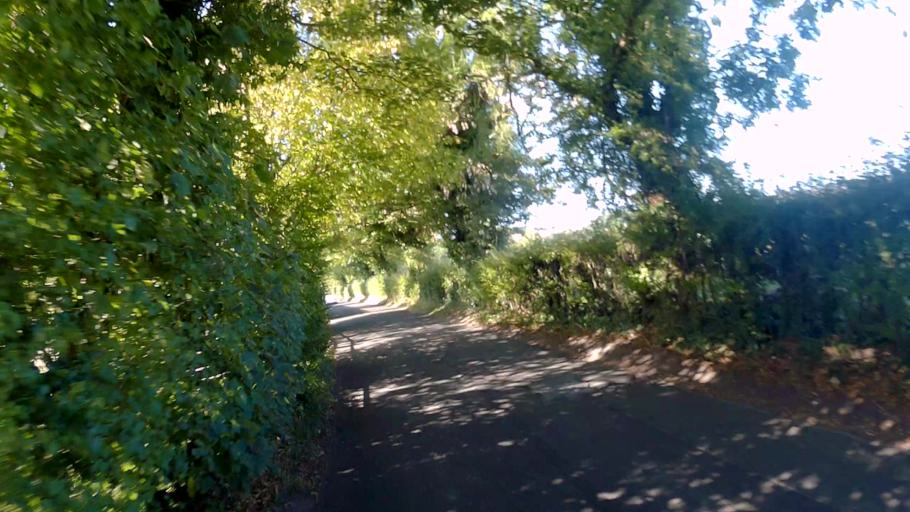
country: GB
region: England
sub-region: Hampshire
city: Long Sutton
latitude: 51.1869
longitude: -0.9015
